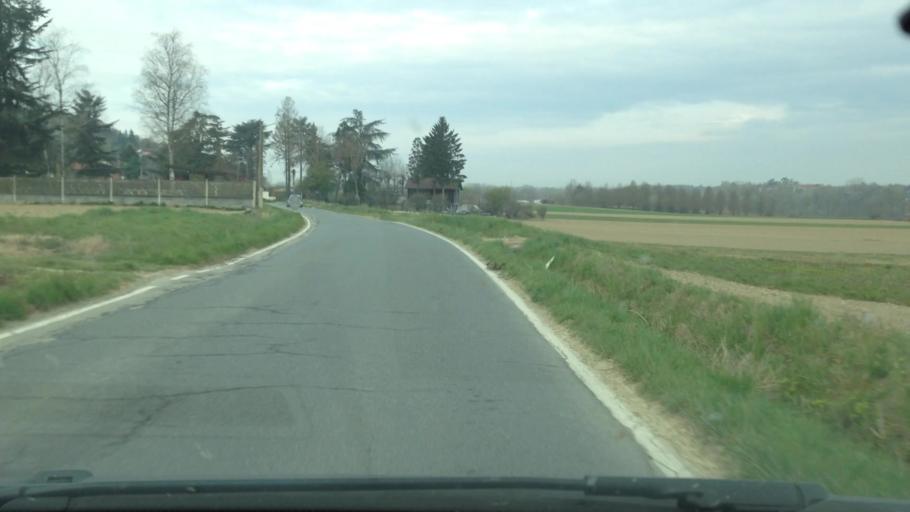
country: IT
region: Piedmont
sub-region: Provincia di Asti
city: Asti
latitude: 44.8947
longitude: 8.1771
